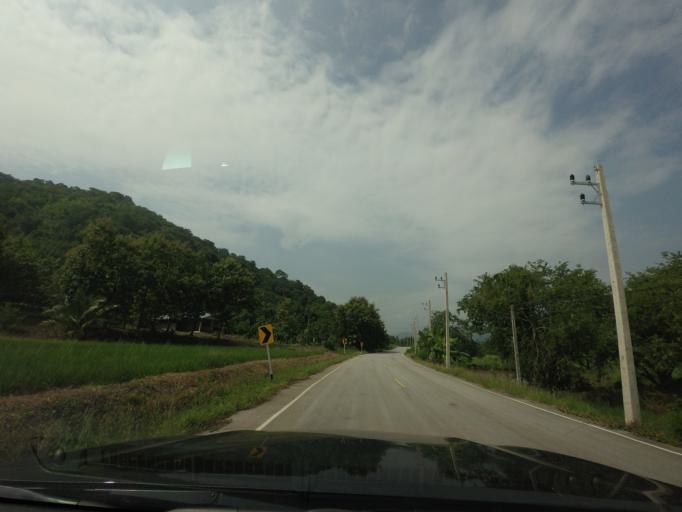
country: LA
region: Xiagnabouli
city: Muang Kenthao
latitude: 17.6786
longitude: 101.3714
